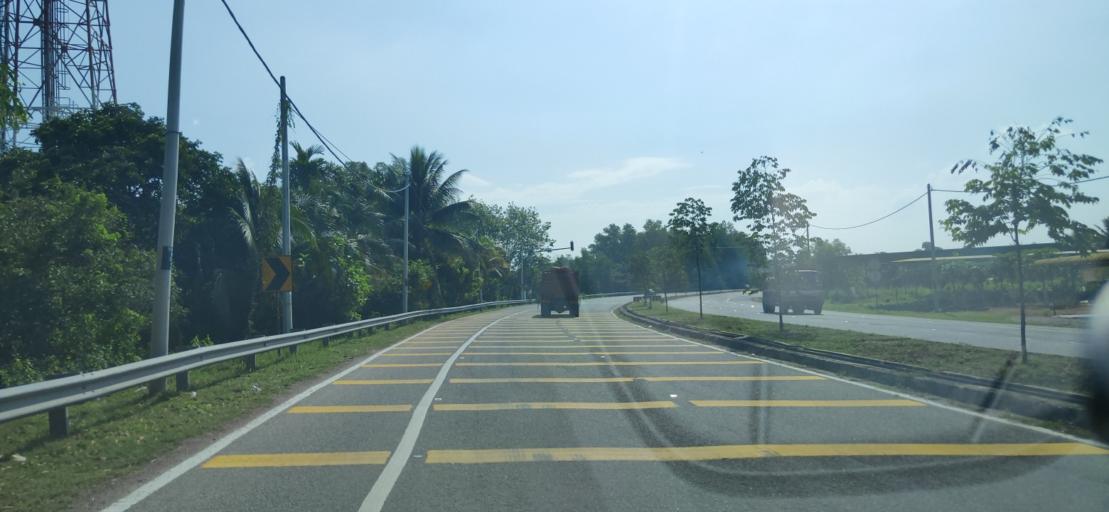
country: MY
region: Kedah
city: Sungai Petani
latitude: 5.6740
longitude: 100.4663
